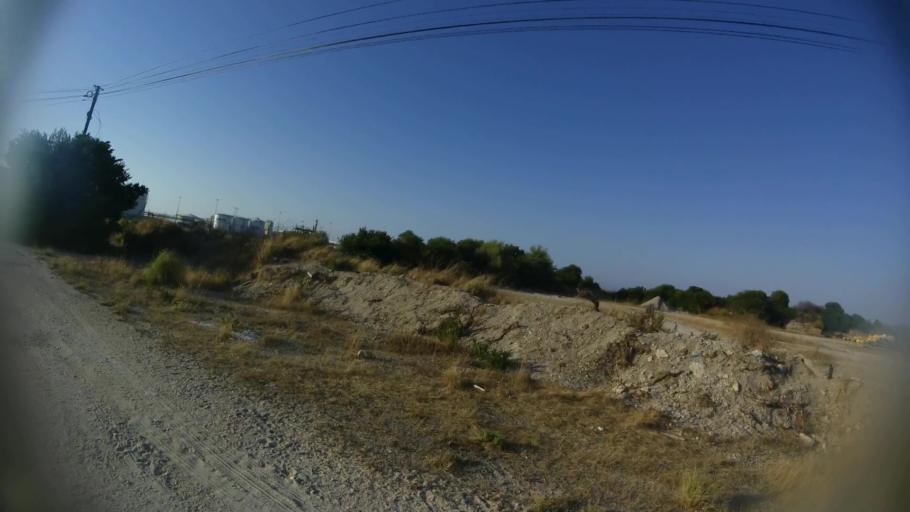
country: PT
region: Aveiro
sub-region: Ilhavo
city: Gafanha da Nazare
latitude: 40.6498
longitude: -8.7032
